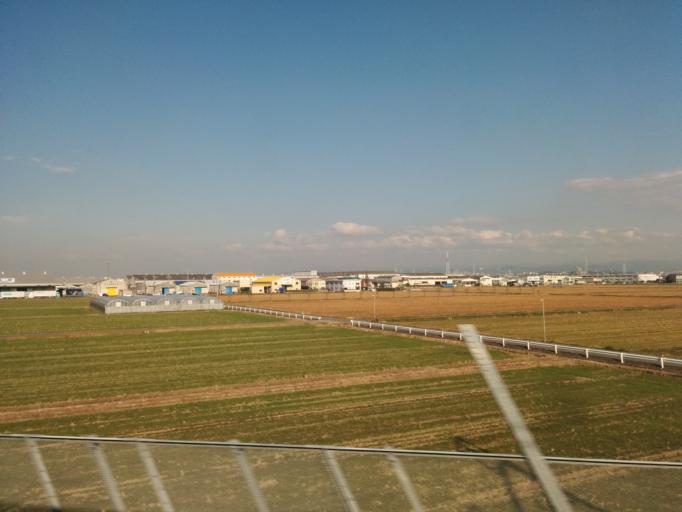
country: JP
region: Aichi
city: Okazaki
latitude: 34.9014
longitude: 137.1228
